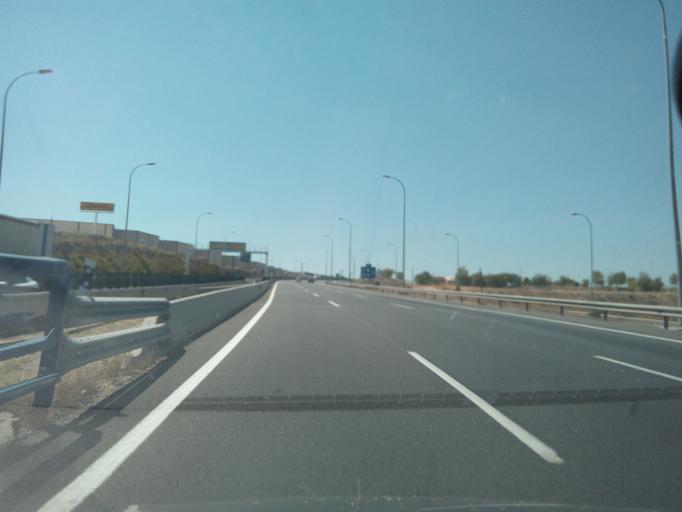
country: ES
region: Madrid
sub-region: Provincia de Madrid
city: Ciempozuelos
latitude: 40.1018
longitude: -3.6367
